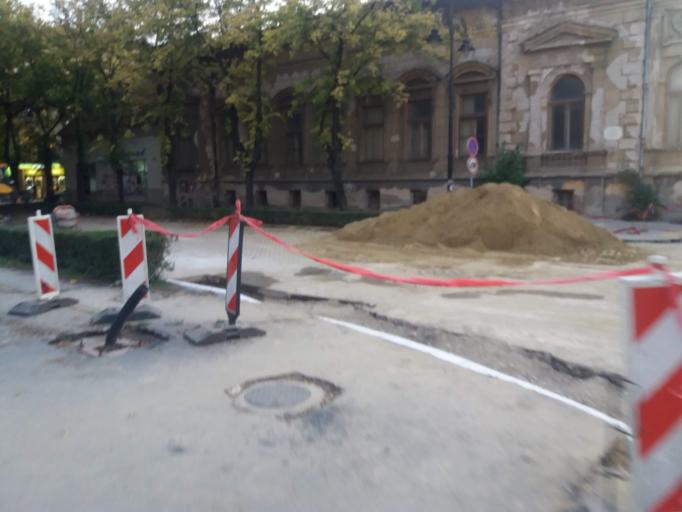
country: RS
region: Autonomna Pokrajina Vojvodina
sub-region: Severnobacki Okrug
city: Subotica
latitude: 46.0981
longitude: 19.6670
